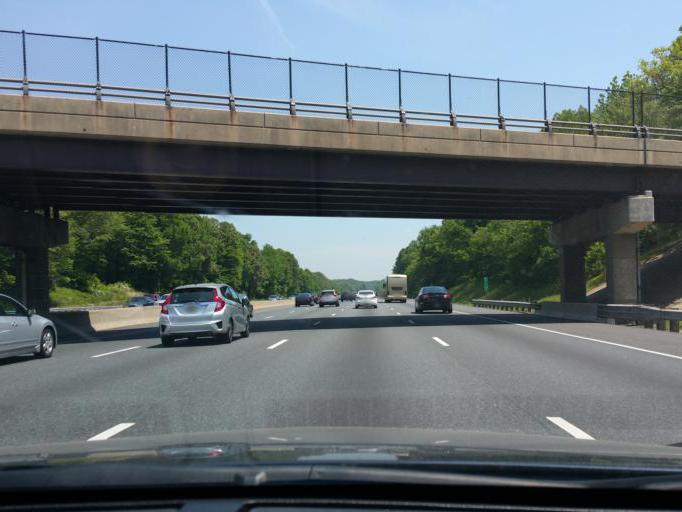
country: US
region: Maryland
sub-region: Baltimore County
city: Kingsville
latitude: 39.4277
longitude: -76.3890
